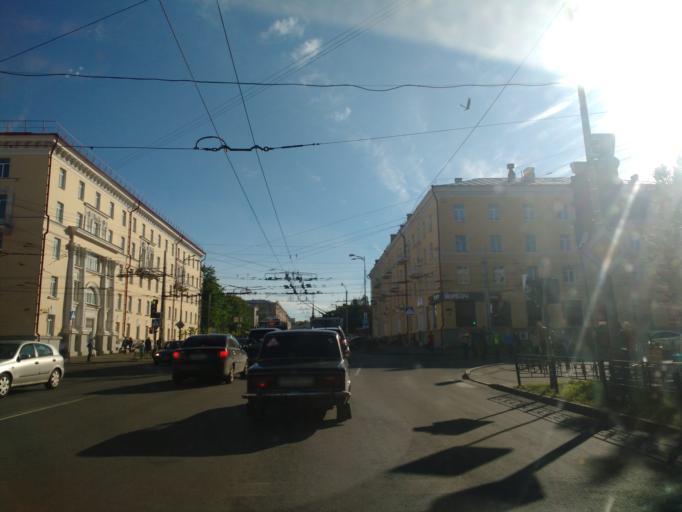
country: RU
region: Republic of Karelia
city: Petrozavodsk
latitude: 61.7875
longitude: 34.3551
